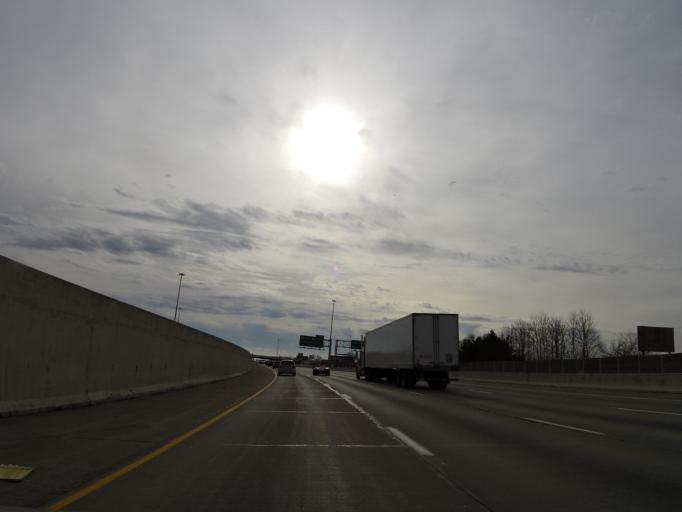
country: US
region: Indiana
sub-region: Marion County
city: Lawrence
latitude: 39.8515
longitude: -86.0468
